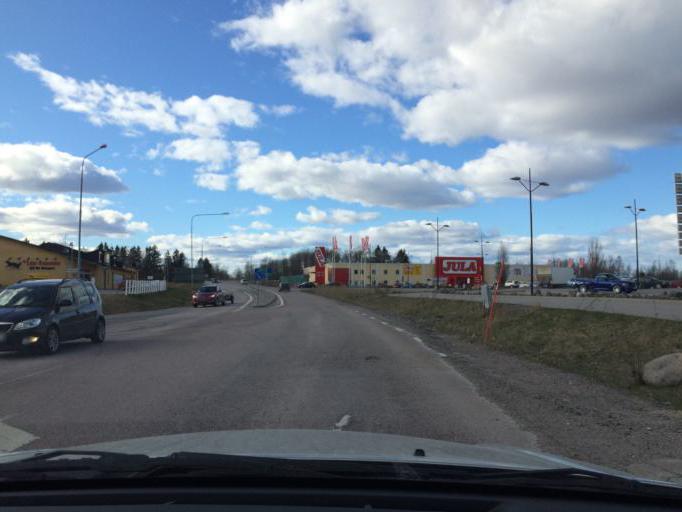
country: SE
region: Soedermanland
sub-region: Eskilstuna Kommun
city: Hallbybrunn
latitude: 59.4024
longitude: 16.4243
